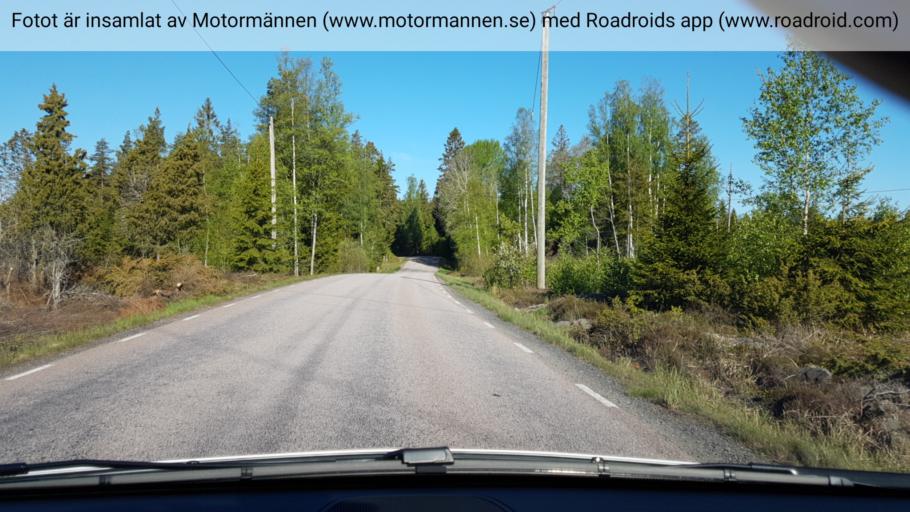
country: SE
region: Vaestra Goetaland
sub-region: Skovde Kommun
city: Stopen
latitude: 58.5410
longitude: 13.6915
